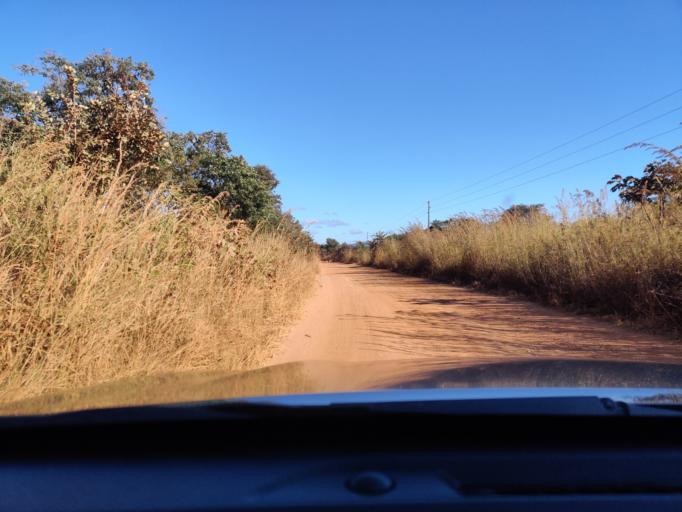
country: ZM
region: Central
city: Mkushi
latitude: -13.5973
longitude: 29.3687
